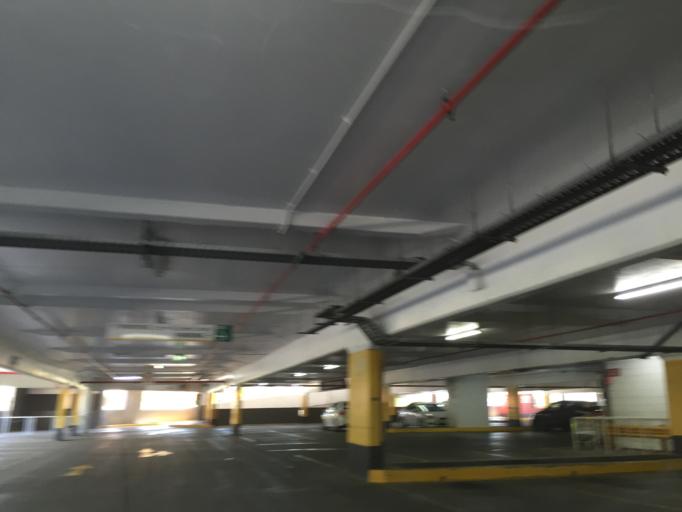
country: AU
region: New South Wales
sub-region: Blacktown
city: Blacktown
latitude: -33.7710
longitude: 150.9046
